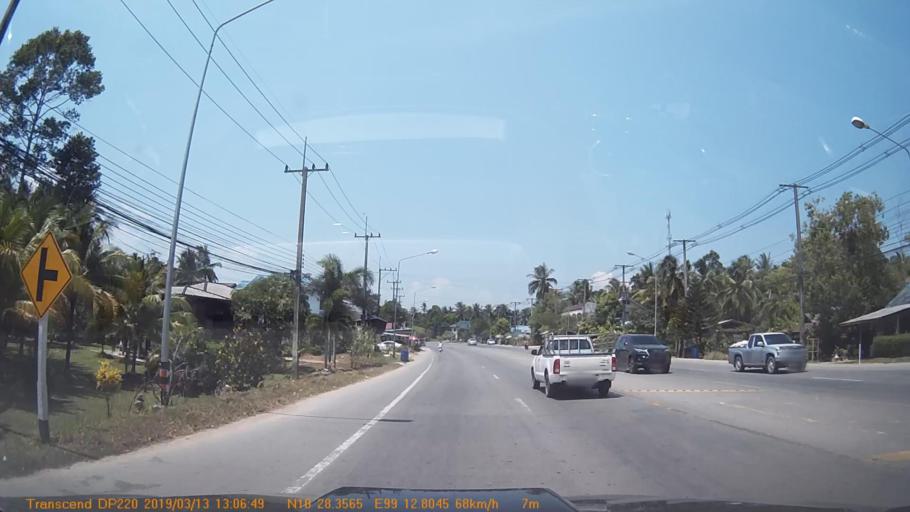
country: TH
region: Chumphon
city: Chumphon
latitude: 10.4730
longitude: 99.2132
